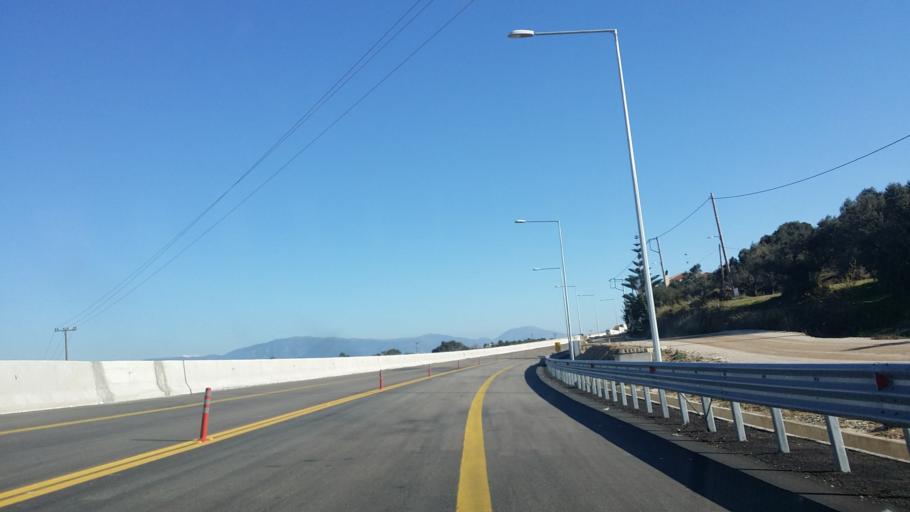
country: GR
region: West Greece
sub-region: Nomos Achaias
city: Ano Kastritsion
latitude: 38.3228
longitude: 21.8396
